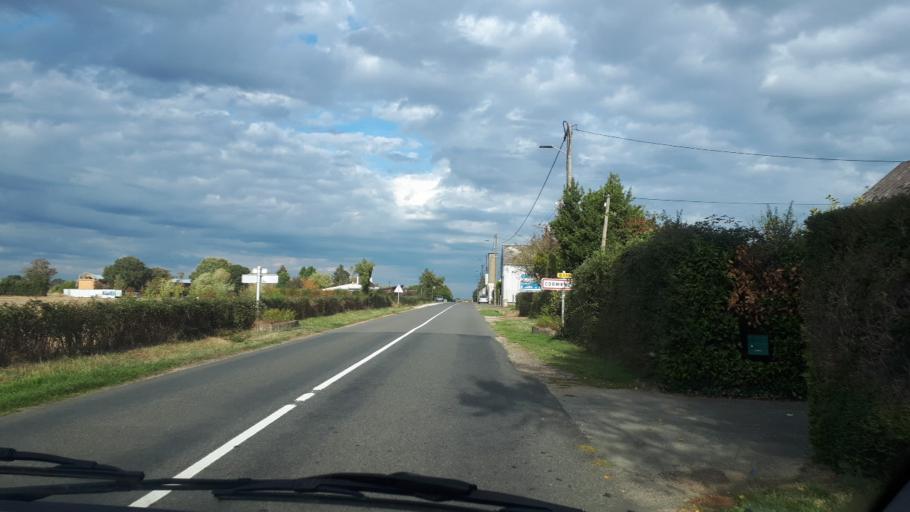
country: FR
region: Centre
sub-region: Departement du Loir-et-Cher
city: Mondoubleau
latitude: 47.9764
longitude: 0.9042
